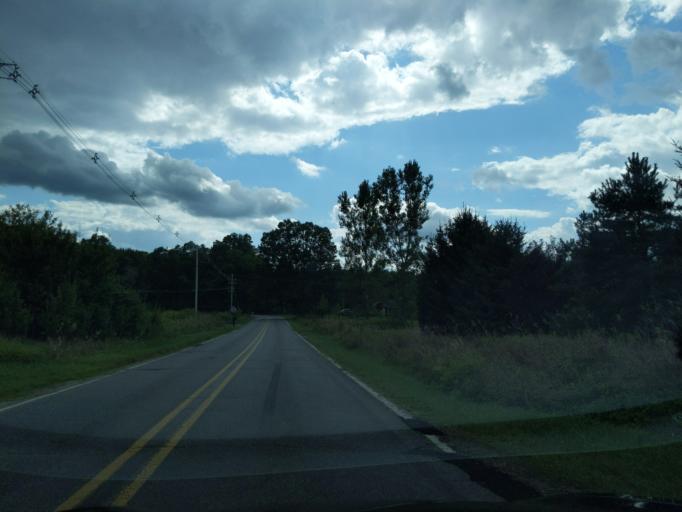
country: US
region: Michigan
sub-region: Ingham County
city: Leslie
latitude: 42.3661
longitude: -84.5467
